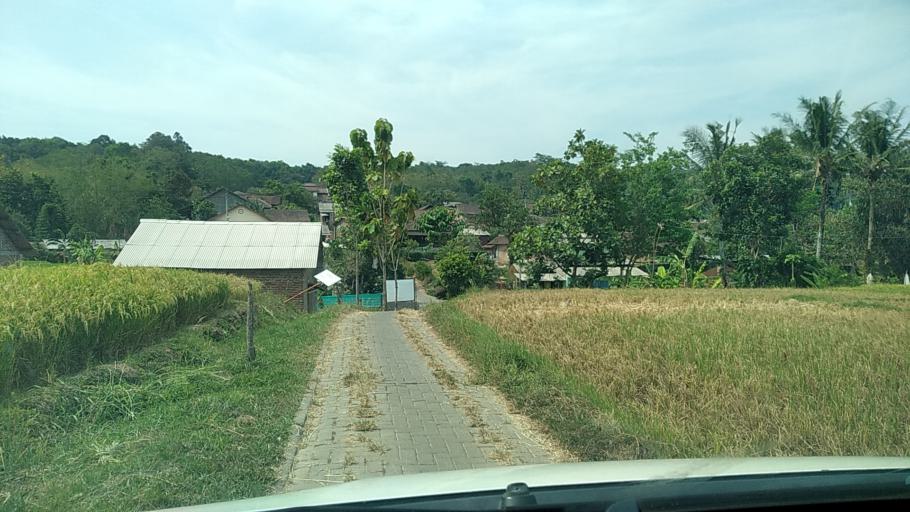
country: ID
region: Central Java
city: Ungaran
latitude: -7.0792
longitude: 110.3174
